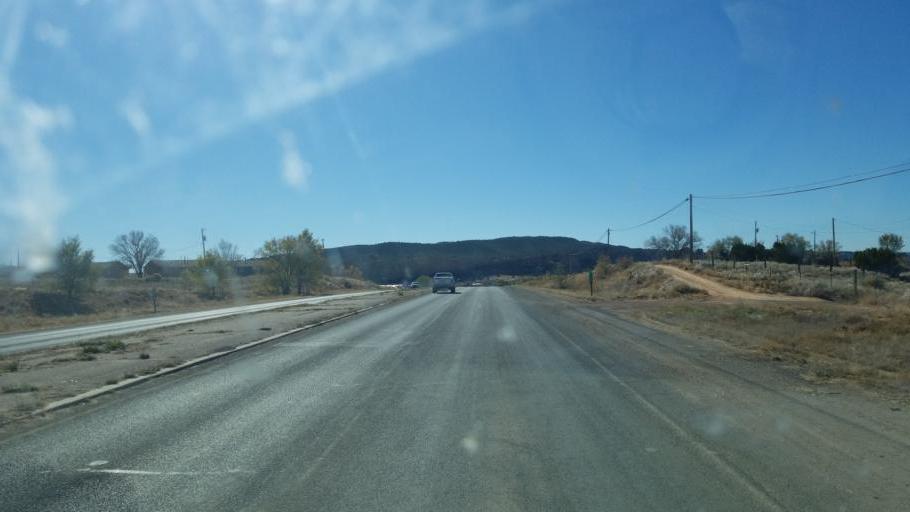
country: US
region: Arizona
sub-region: Apache County
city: Window Rock
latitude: 35.6692
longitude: -109.0591
